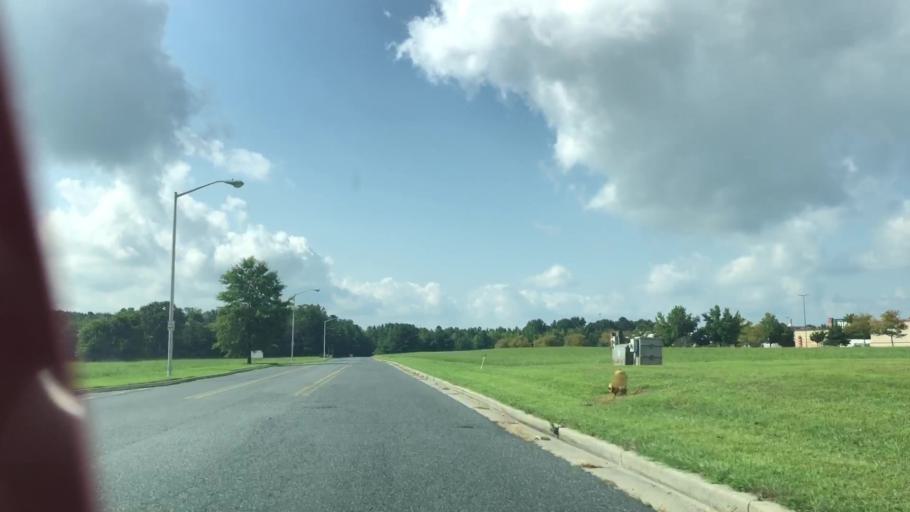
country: US
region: Maryland
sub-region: Wicomico County
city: Salisbury
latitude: 38.4004
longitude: -75.5627
